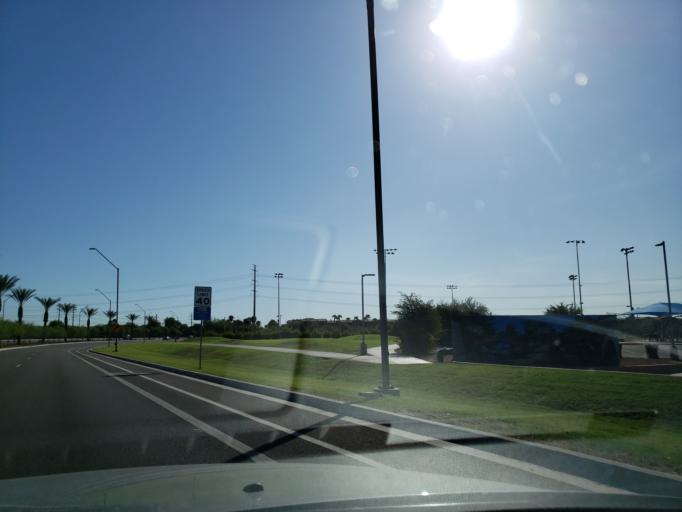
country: US
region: Arizona
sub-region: Maricopa County
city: Avondale
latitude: 33.4629
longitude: -112.3222
